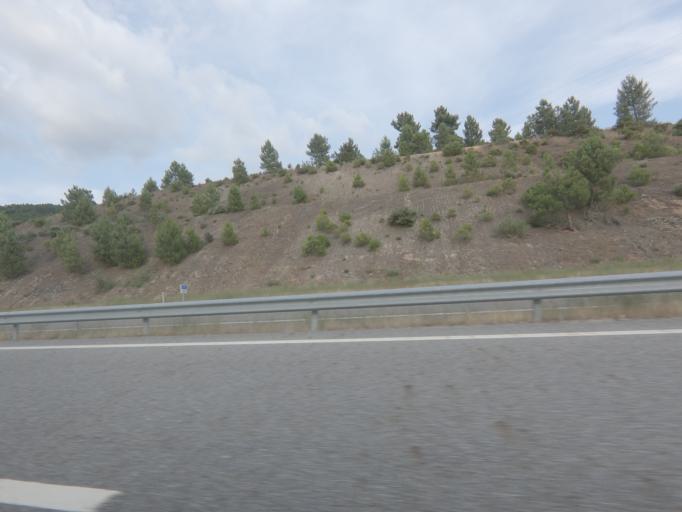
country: PT
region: Vila Real
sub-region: Boticas
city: Boticas
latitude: 41.6738
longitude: -7.5674
